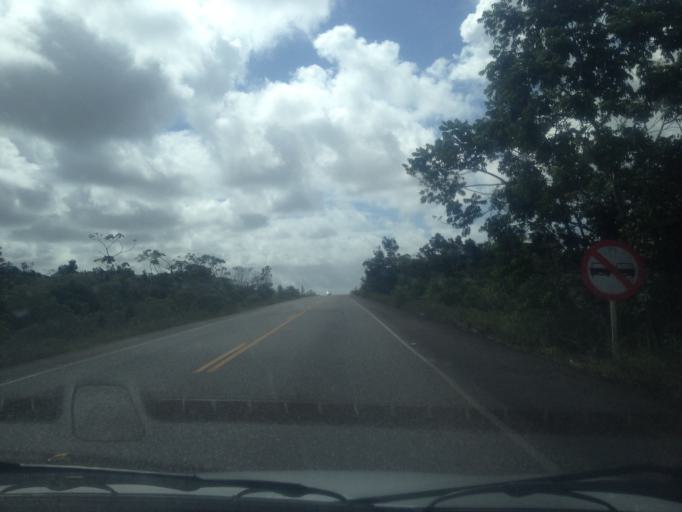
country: BR
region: Bahia
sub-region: Entre Rios
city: Entre Rios
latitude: -12.2648
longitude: -37.8723
